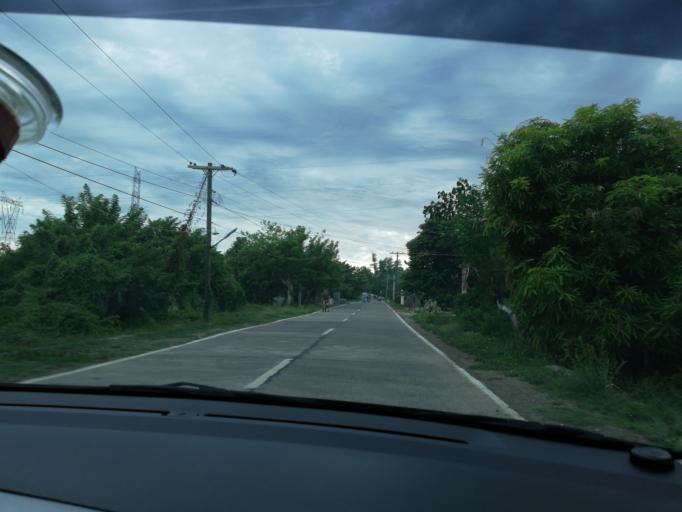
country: PH
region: Ilocos
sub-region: Province of Ilocos Sur
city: Narvacan
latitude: 17.4198
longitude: 120.4664
